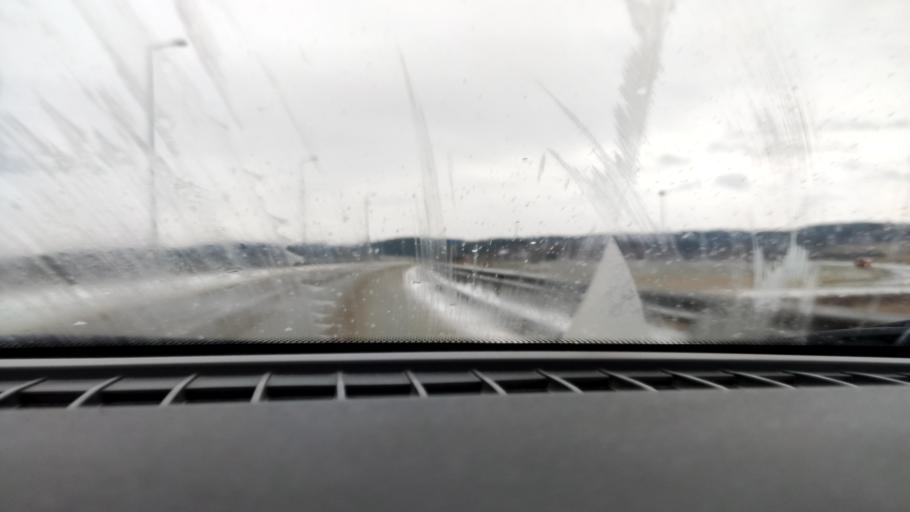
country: RU
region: Perm
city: Kondratovo
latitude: 57.9279
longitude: 56.1727
